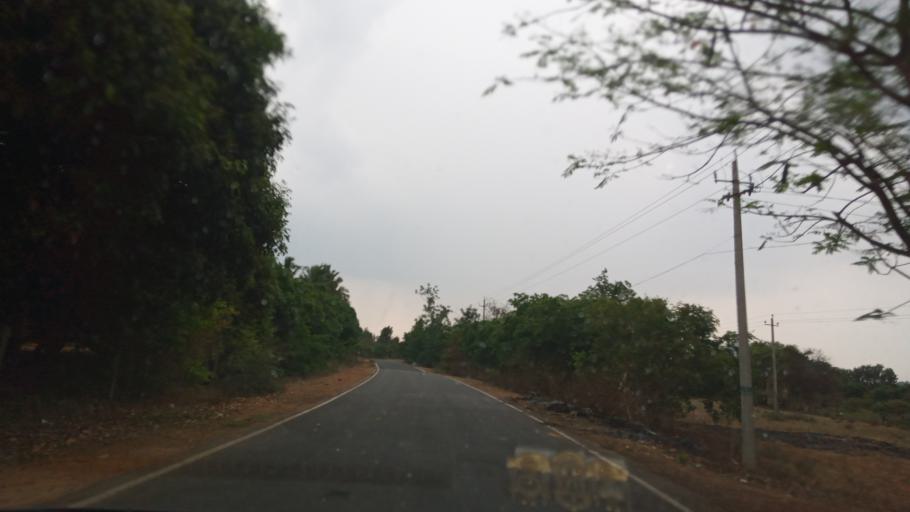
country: IN
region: Karnataka
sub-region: Kolar
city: Mulbagal
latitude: 13.1272
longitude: 78.3501
